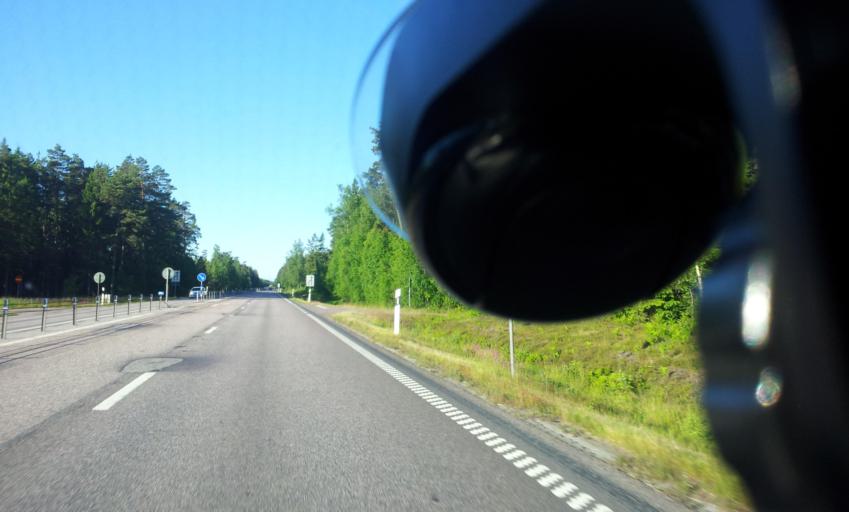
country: SE
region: Kalmar
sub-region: Monsteras Kommun
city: Moensteras
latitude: 57.0071
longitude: 16.4208
